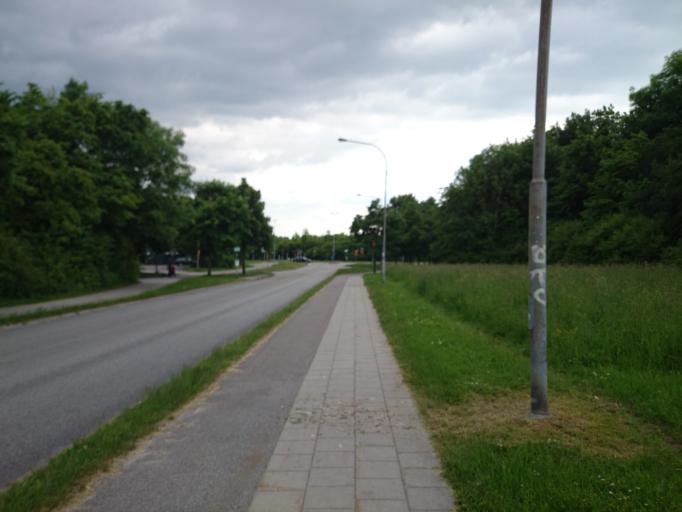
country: SE
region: Skane
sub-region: Lunds Kommun
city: Lund
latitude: 55.7111
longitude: 13.2227
